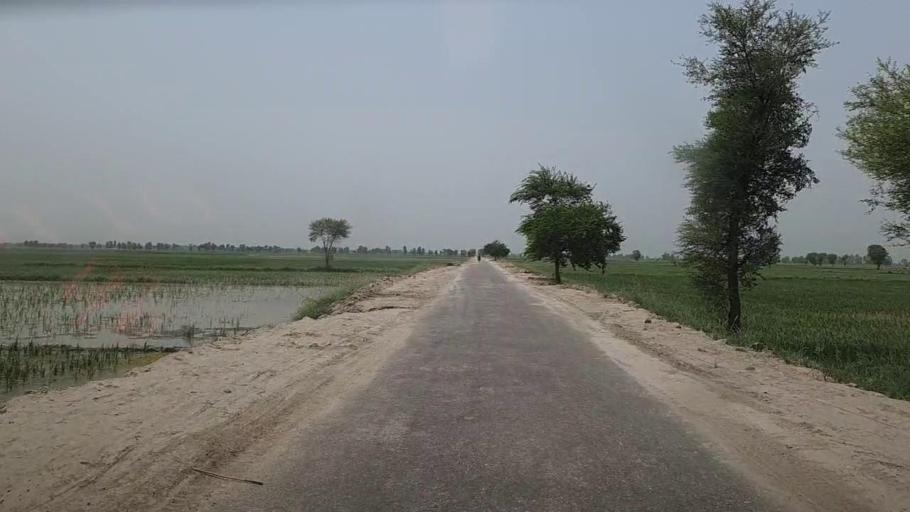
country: PK
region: Sindh
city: Sita Road
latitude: 27.0816
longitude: 67.9105
